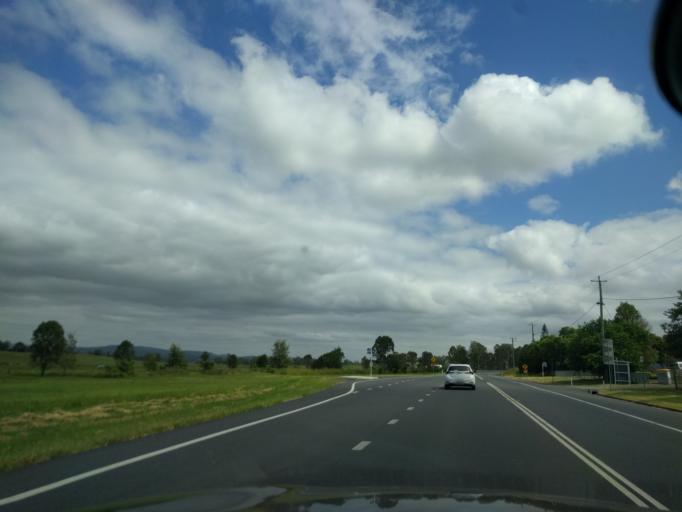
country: AU
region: Queensland
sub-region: Logan
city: Cedar Vale
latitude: -27.8938
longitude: 152.9737
